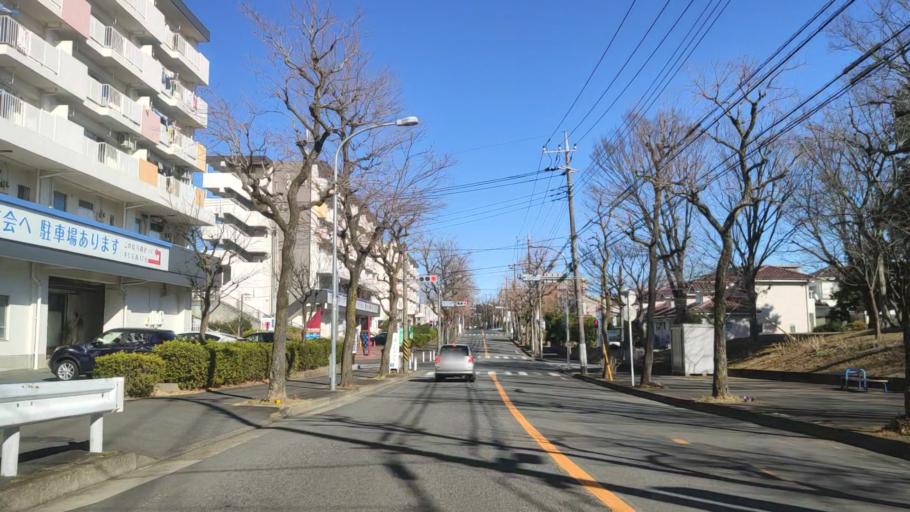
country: JP
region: Tokyo
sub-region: Machida-shi
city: Machida
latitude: 35.5132
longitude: 139.5042
